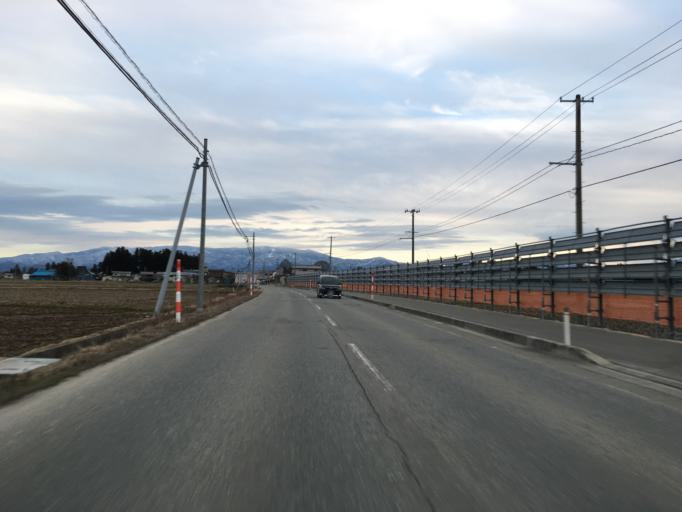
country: JP
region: Yamagata
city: Yonezawa
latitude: 37.9875
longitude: 140.0765
